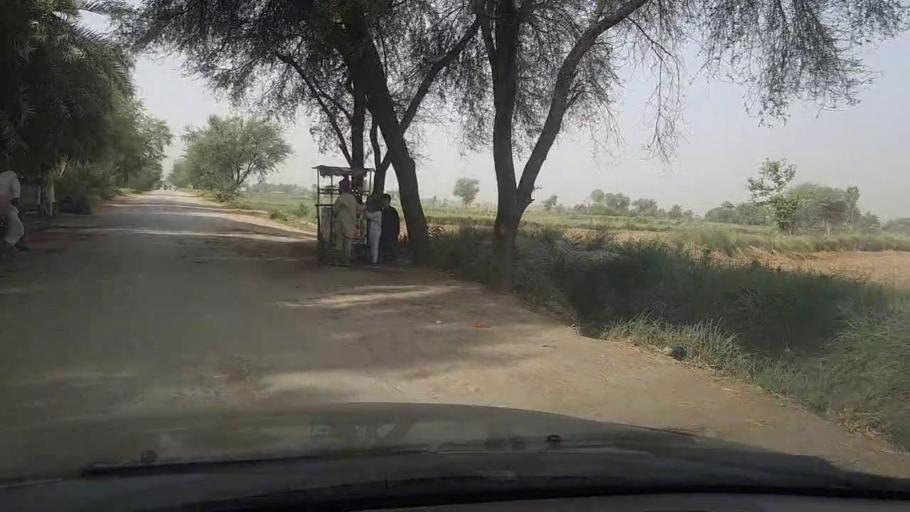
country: PK
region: Sindh
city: Shikarpur
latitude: 27.9243
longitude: 68.6135
